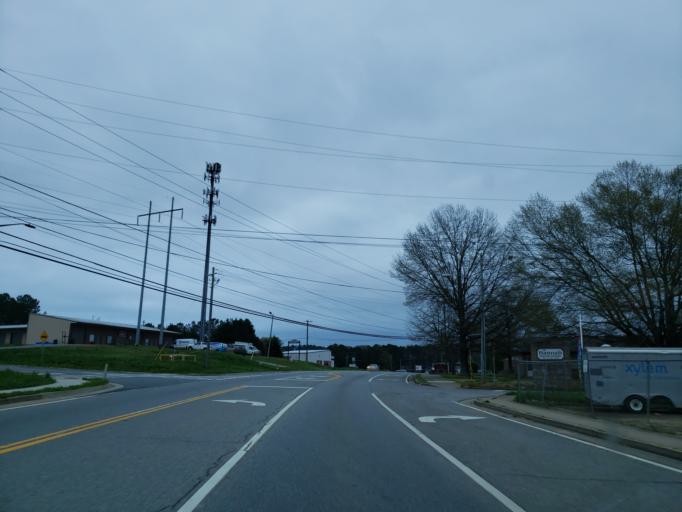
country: US
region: Georgia
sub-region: Bartow County
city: Cartersville
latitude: 34.1511
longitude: -84.8207
